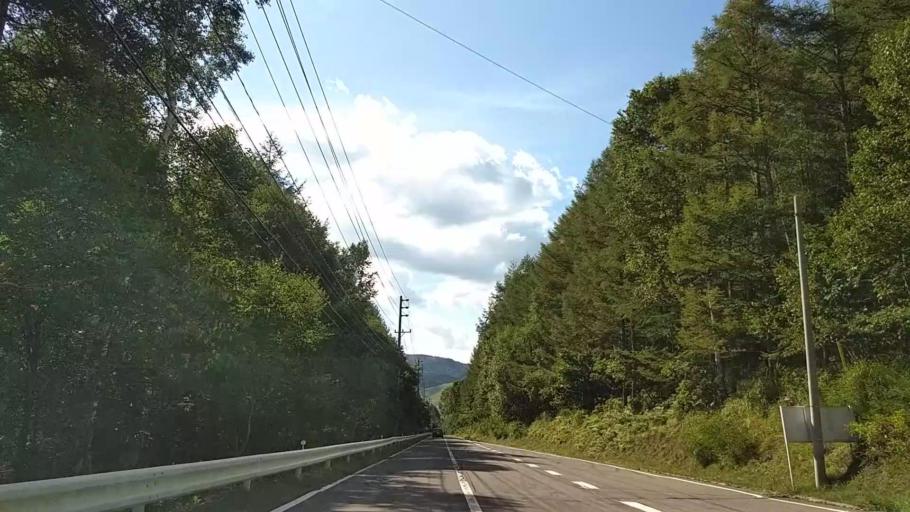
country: JP
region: Nagano
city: Chino
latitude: 36.0995
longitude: 138.2551
